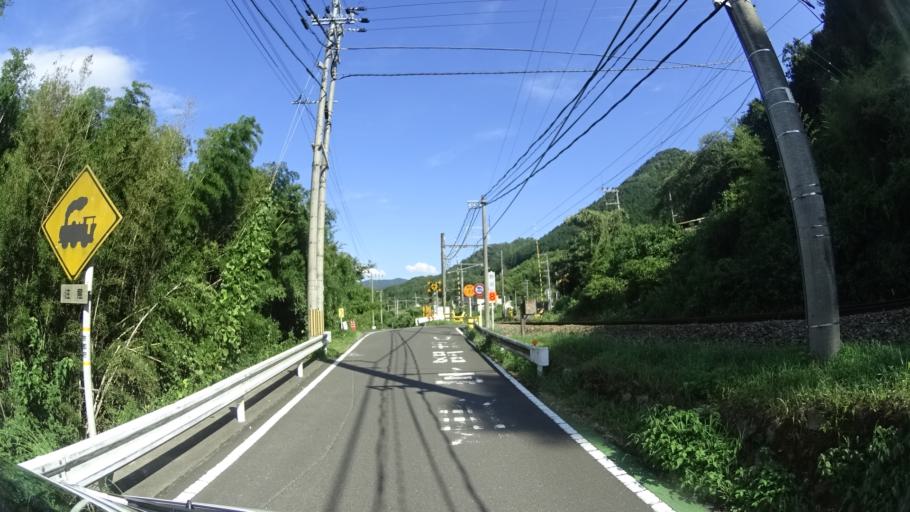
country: JP
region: Kyoto
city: Ayabe
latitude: 35.2896
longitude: 135.2693
